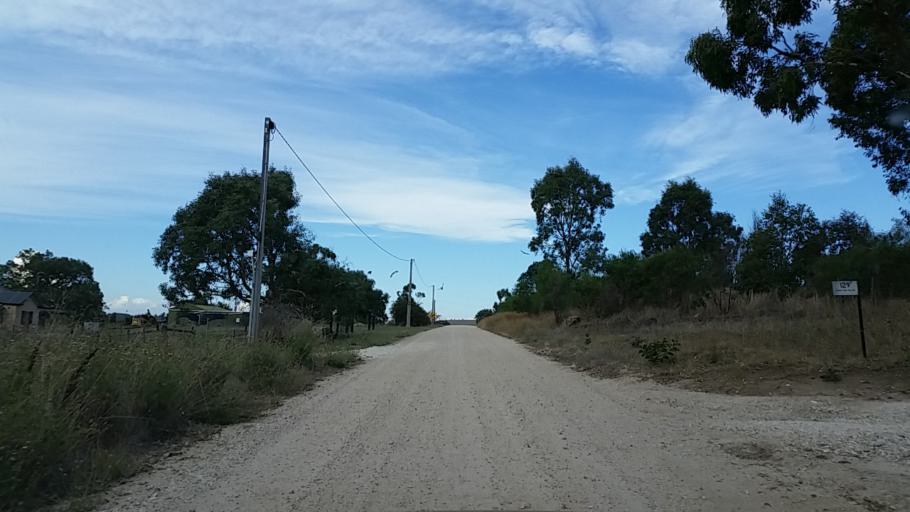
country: AU
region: South Australia
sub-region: Barossa
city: Angaston
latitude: -34.5624
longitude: 139.0769
